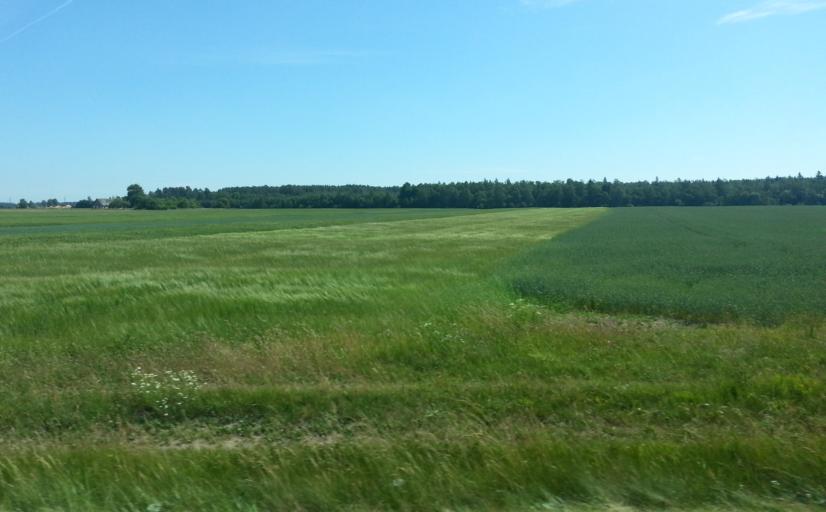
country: LT
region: Panevezys
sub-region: Panevezys City
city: Panevezys
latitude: 55.8405
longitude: 24.3581
